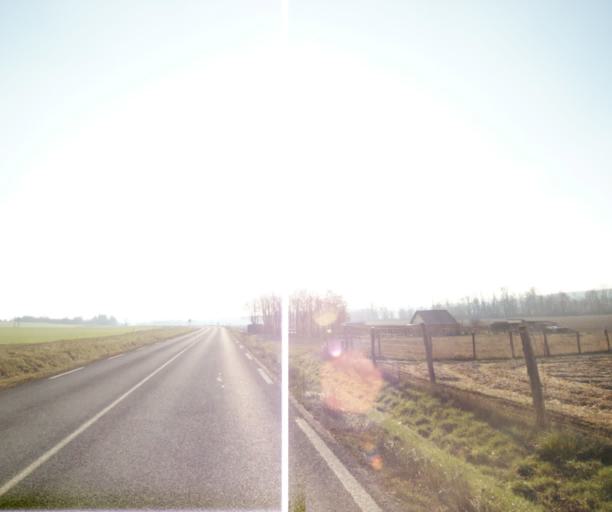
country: FR
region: Champagne-Ardenne
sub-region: Departement de la Haute-Marne
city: Wassy
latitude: 48.5121
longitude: 4.9373
